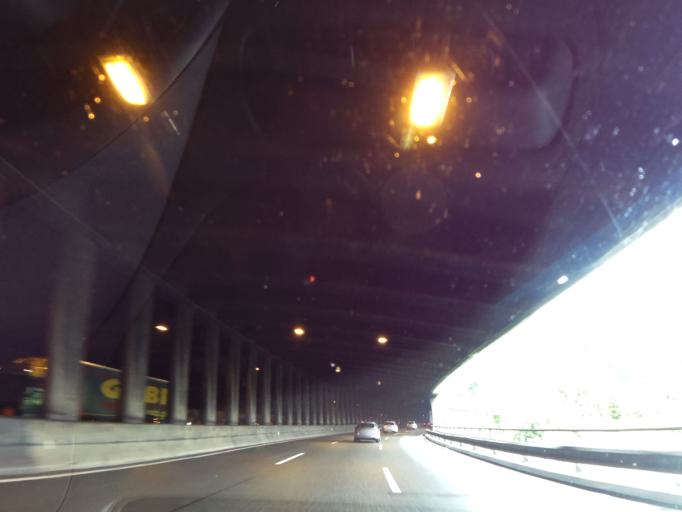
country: AT
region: Tyrol
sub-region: Politischer Bezirk Innsbruck Land
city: Schoenberg im Stubaital
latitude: 47.1900
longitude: 11.4010
